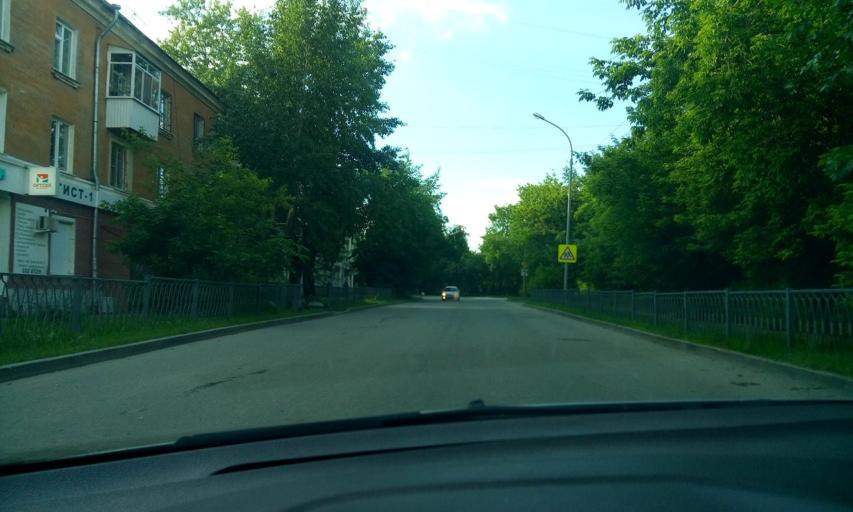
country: RU
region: Sverdlovsk
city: Yekaterinburg
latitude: 56.8858
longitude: 60.5698
